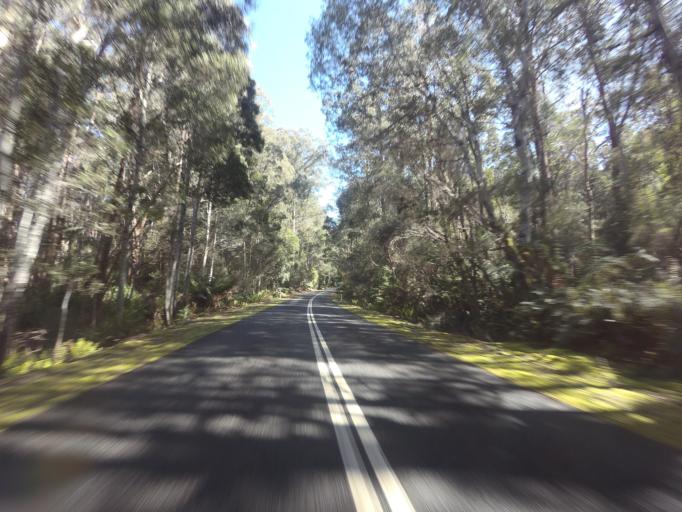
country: AU
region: Tasmania
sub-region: Derwent Valley
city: New Norfolk
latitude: -42.7535
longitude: 146.5240
